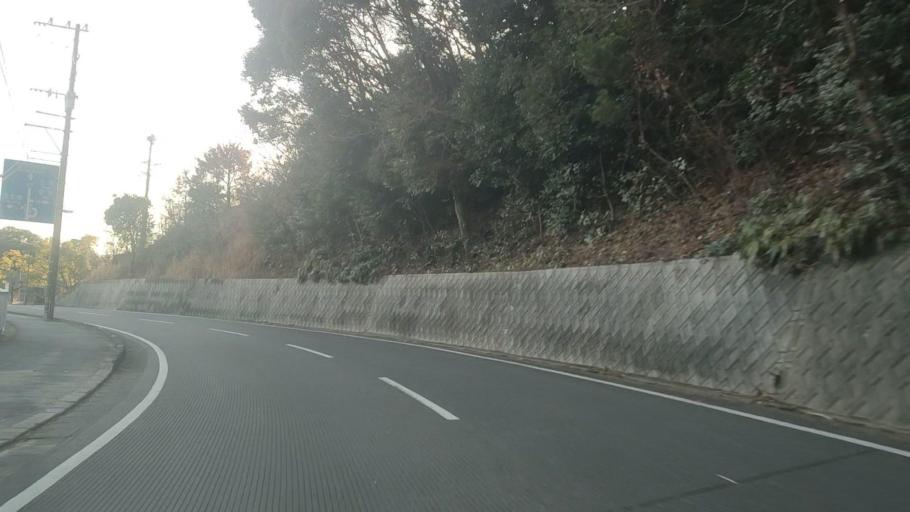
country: JP
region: Fukuoka
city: Dazaifu
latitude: 33.5275
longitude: 130.5439
